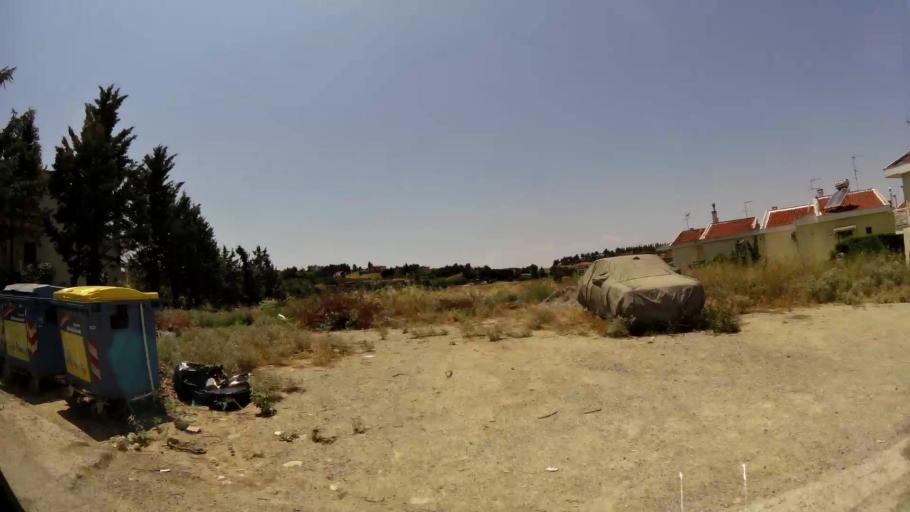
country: GR
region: Central Macedonia
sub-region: Nomos Thessalonikis
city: Plagiari
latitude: 40.4746
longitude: 22.9540
